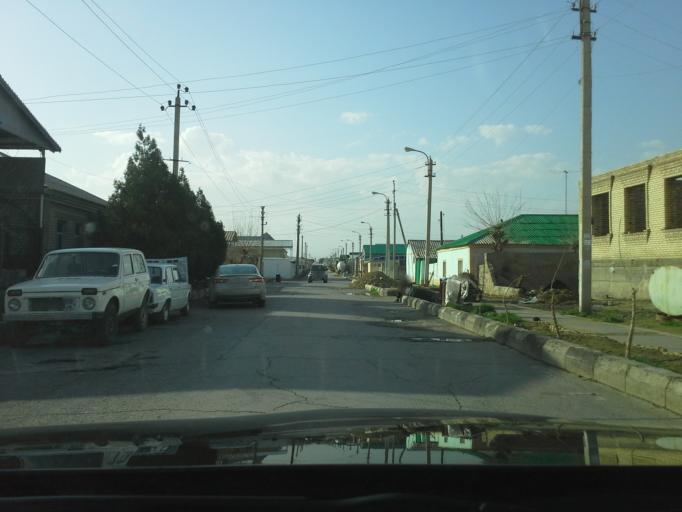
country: TM
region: Ahal
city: Abadan
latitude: 38.0192
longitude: 58.2319
